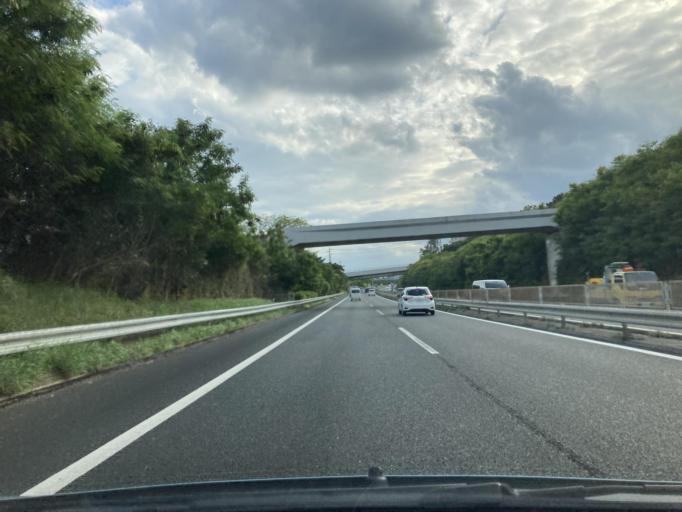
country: JP
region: Okinawa
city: Ginowan
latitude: 26.2668
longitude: 127.7745
